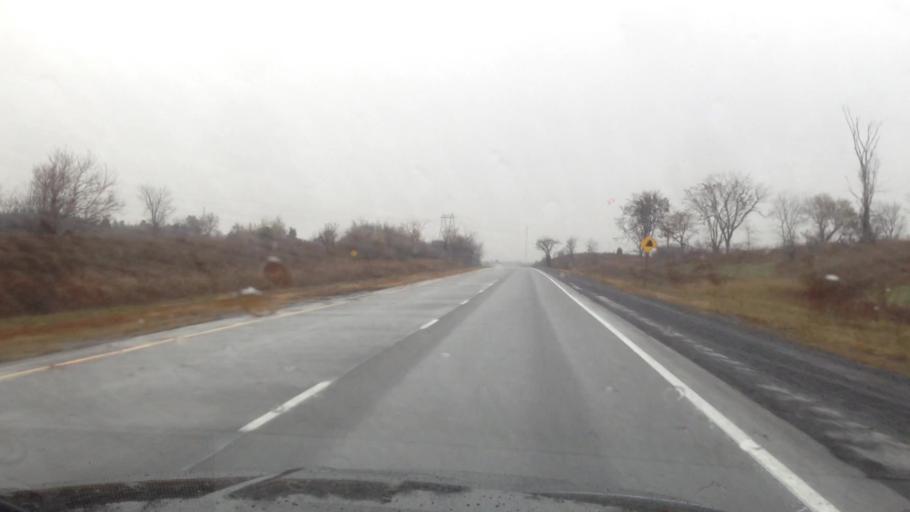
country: CA
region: Ontario
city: Casselman
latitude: 45.3717
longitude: -74.8501
